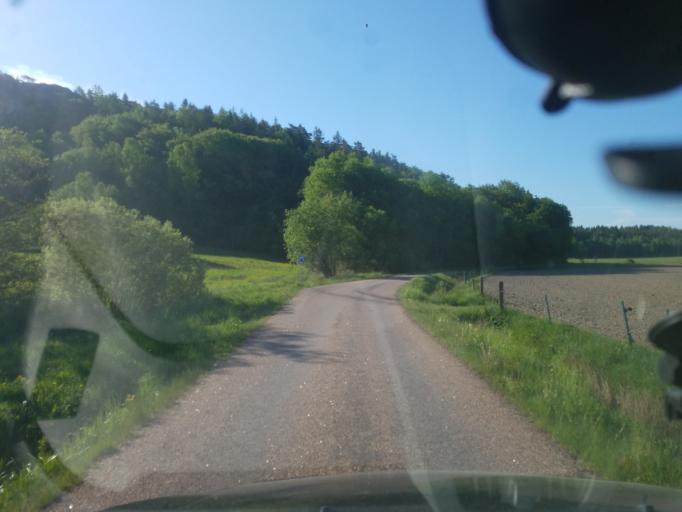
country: SE
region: Vaestra Goetaland
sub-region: Orust
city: Henan
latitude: 58.2874
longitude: 11.6399
